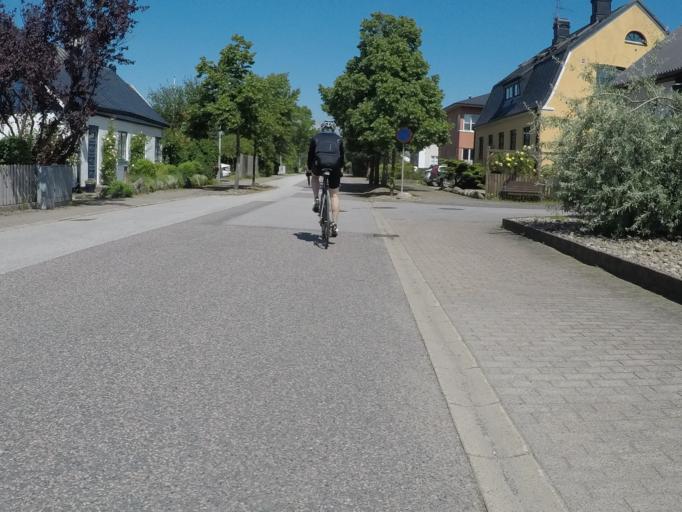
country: SE
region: Skane
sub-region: Lomma Kommun
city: Lomma
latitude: 55.6640
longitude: 13.0634
